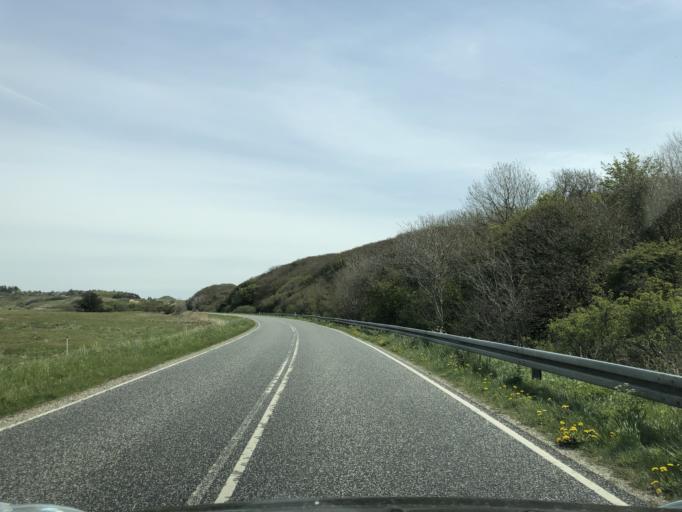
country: DK
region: Central Jutland
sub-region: Struer Kommune
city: Struer
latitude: 56.5416
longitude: 8.5049
